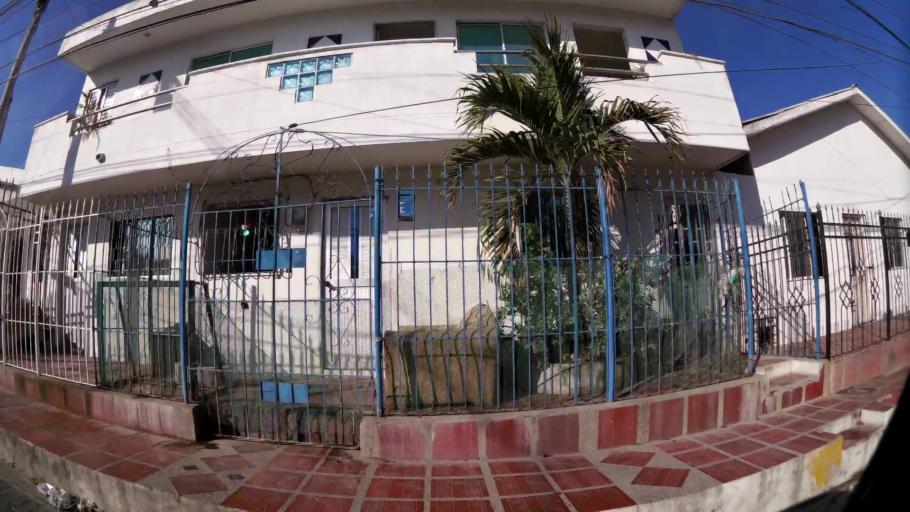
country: CO
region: Atlantico
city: Barranquilla
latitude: 10.9928
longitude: -74.7870
